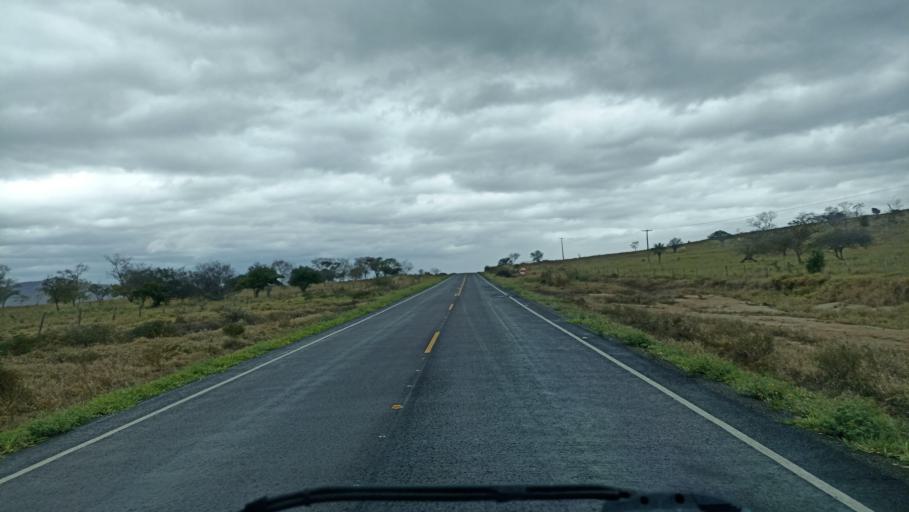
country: BR
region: Bahia
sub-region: Iacu
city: Iacu
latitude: -12.9659
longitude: -40.4897
